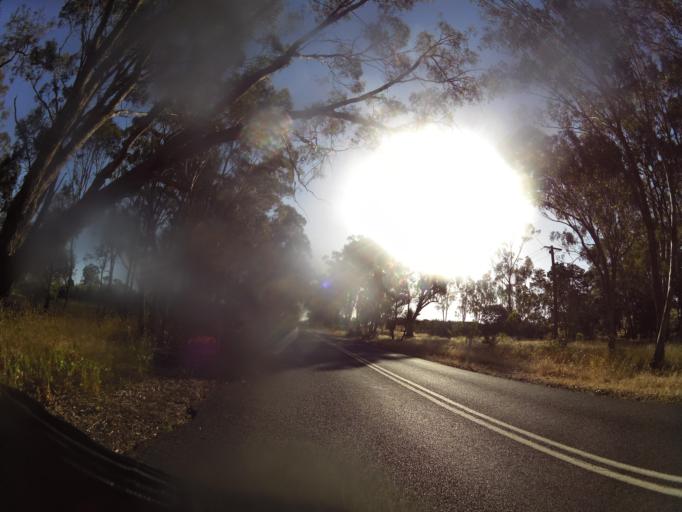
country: AU
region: Victoria
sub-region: Murrindindi
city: Kinglake West
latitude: -37.0206
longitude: 145.1065
